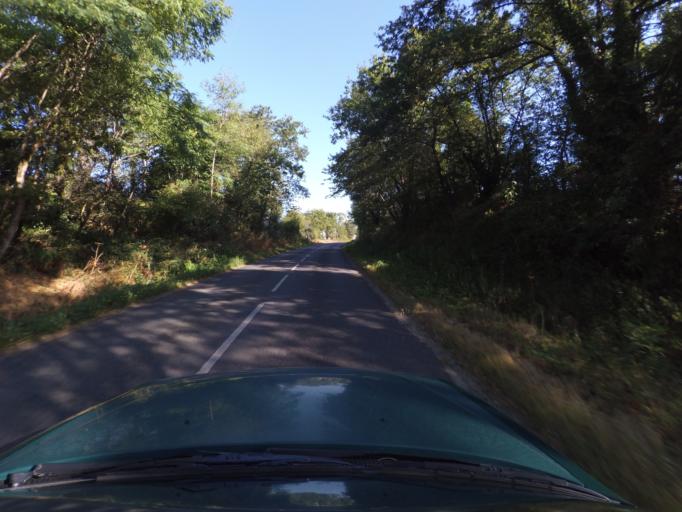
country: FR
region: Pays de la Loire
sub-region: Departement de la Loire-Atlantique
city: Les Sorinieres
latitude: 47.1193
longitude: -1.5255
